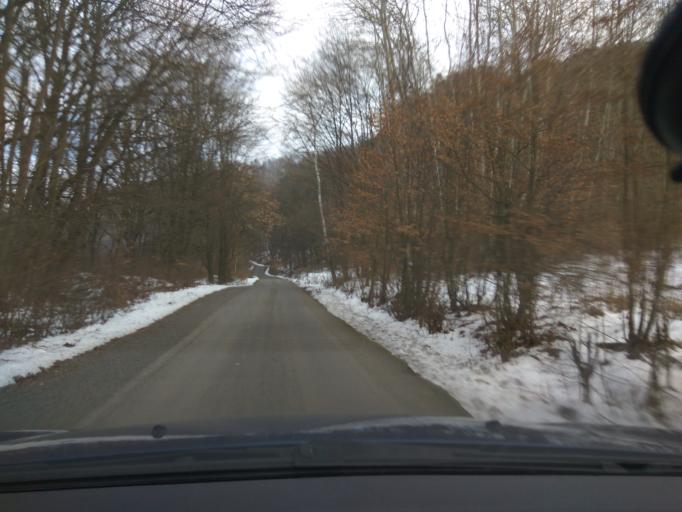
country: SK
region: Banskobystricky
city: Zarnovica
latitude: 48.4710
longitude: 18.7300
